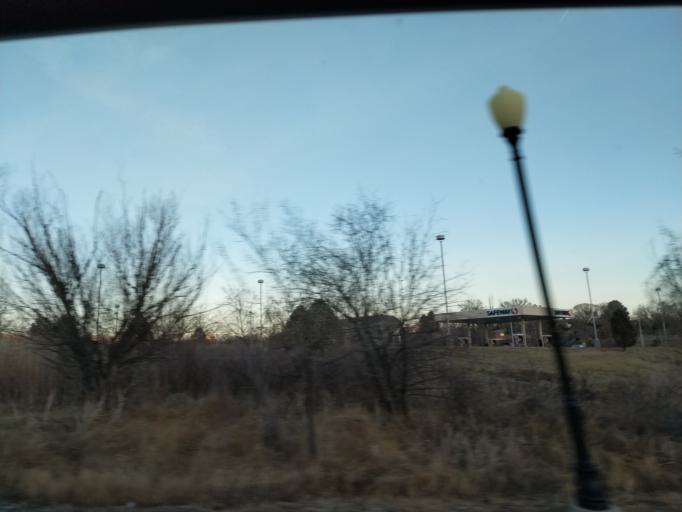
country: US
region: Colorado
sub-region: Mesa County
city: Grand Junction
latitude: 39.1032
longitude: -108.5523
